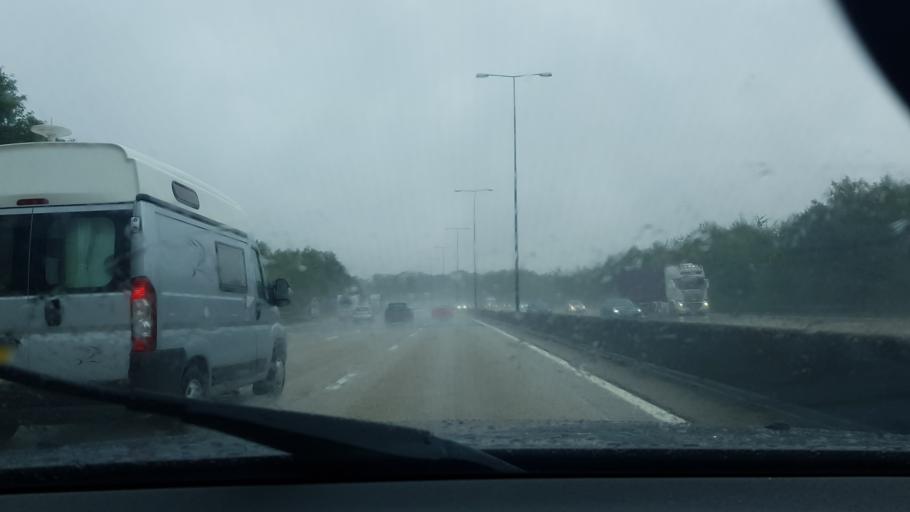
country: GB
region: England
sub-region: Surrey
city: Headley
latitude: 51.2775
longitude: -0.2610
